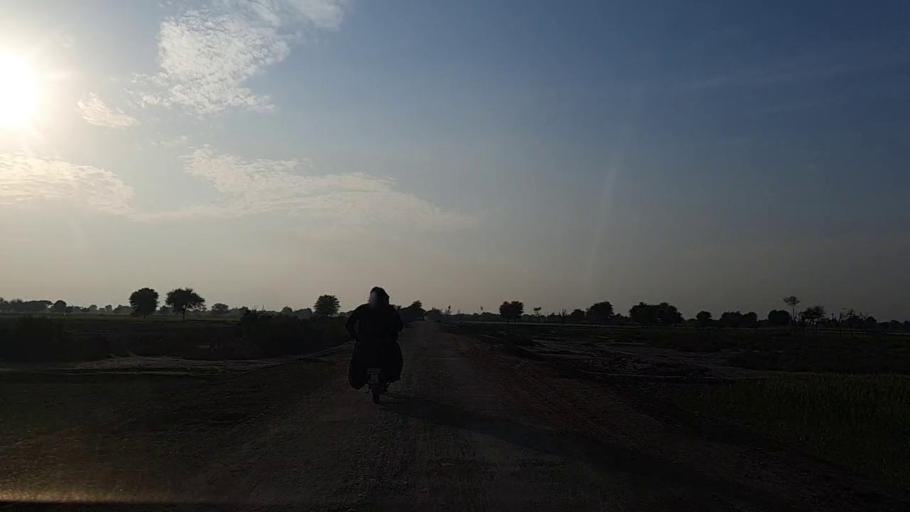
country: PK
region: Sindh
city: Jam Sahib
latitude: 26.3953
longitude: 68.5396
